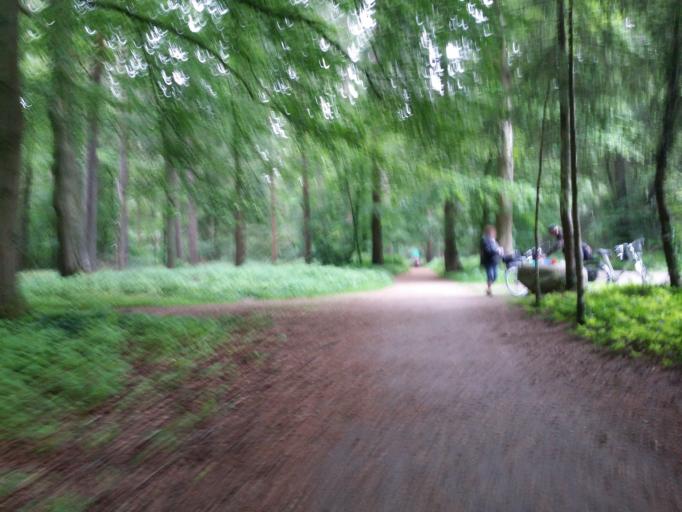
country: DE
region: Lower Saxony
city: Rastede
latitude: 53.2340
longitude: 8.2432
